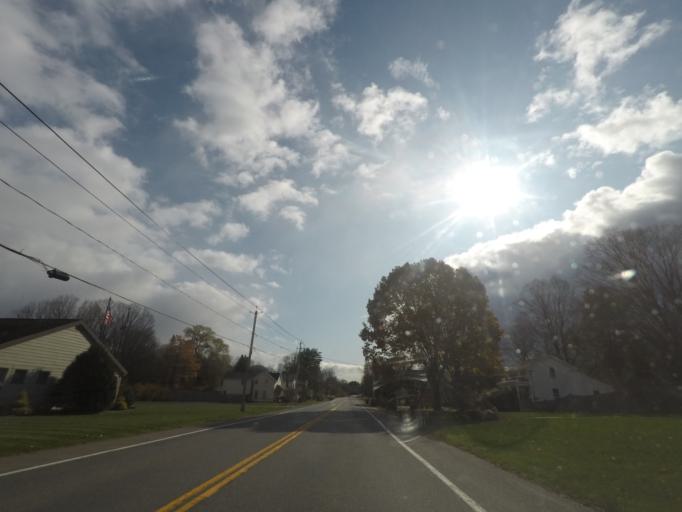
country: US
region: New York
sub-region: Saratoga County
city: Country Knolls
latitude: 42.9057
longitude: -73.8214
